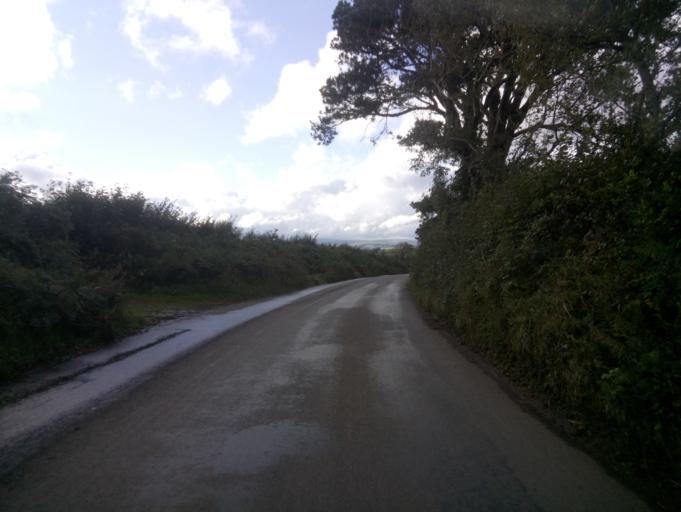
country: GB
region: England
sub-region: Devon
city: South Brent
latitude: 50.3797
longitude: -3.7632
